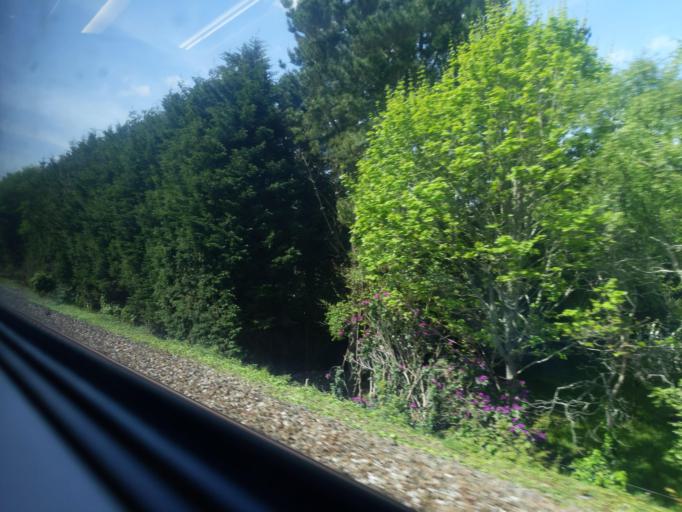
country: GB
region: England
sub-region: Cornwall
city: St Austell
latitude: 50.3387
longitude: -4.7482
